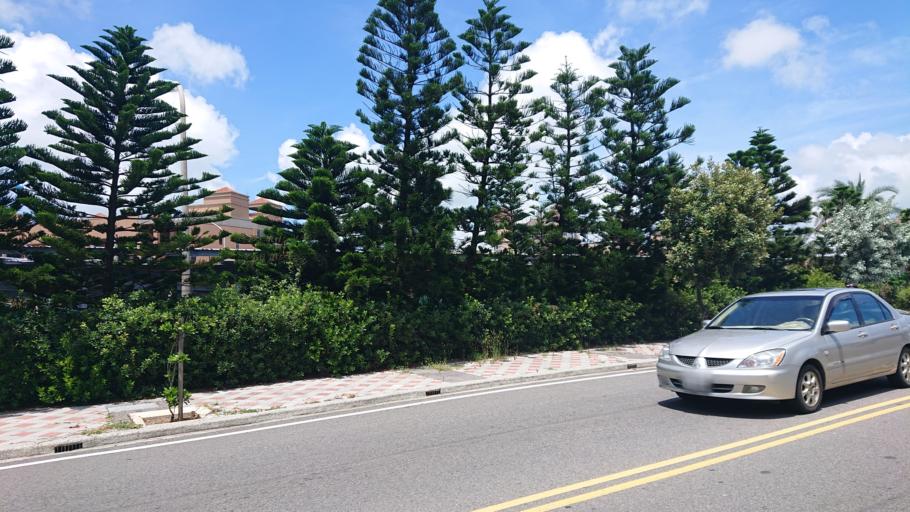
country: TW
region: Taiwan
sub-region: Penghu
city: Ma-kung
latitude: 23.5732
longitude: 119.5815
